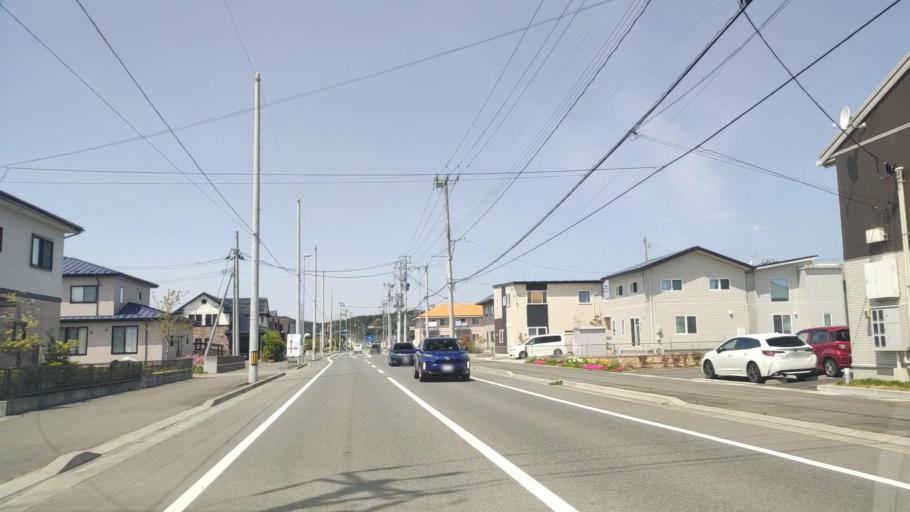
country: JP
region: Aomori
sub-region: Hachinohe Shi
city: Uchimaru
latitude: 40.5148
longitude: 141.4314
